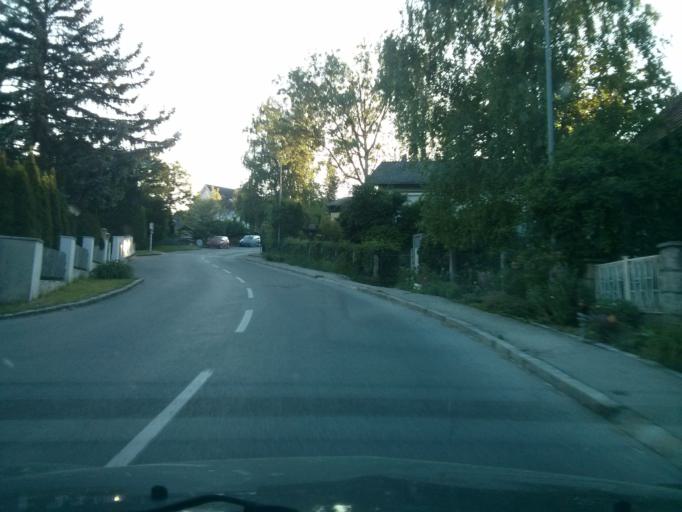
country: AT
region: Lower Austria
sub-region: Politischer Bezirk Baden
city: Hirtenberg
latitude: 47.9112
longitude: 16.1666
